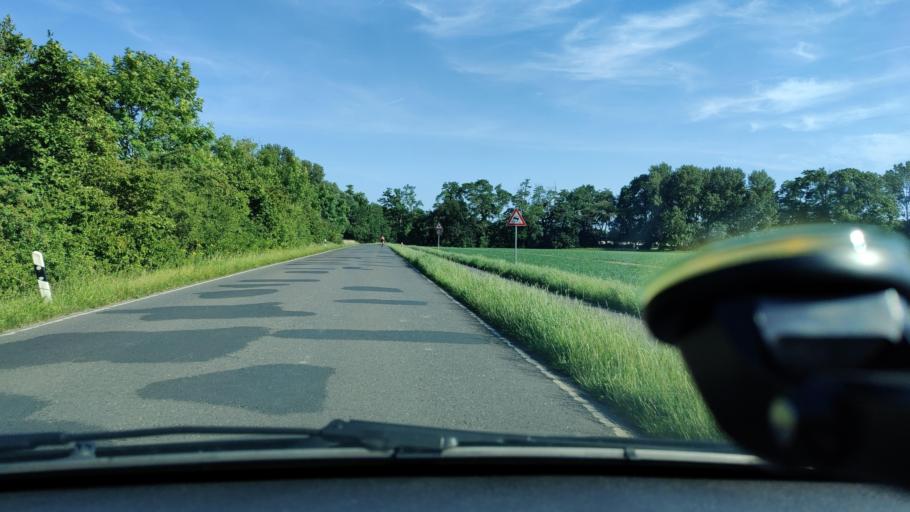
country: DE
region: North Rhine-Westphalia
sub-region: Regierungsbezirk Dusseldorf
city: Kamp-Lintfort
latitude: 51.4927
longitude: 6.5109
